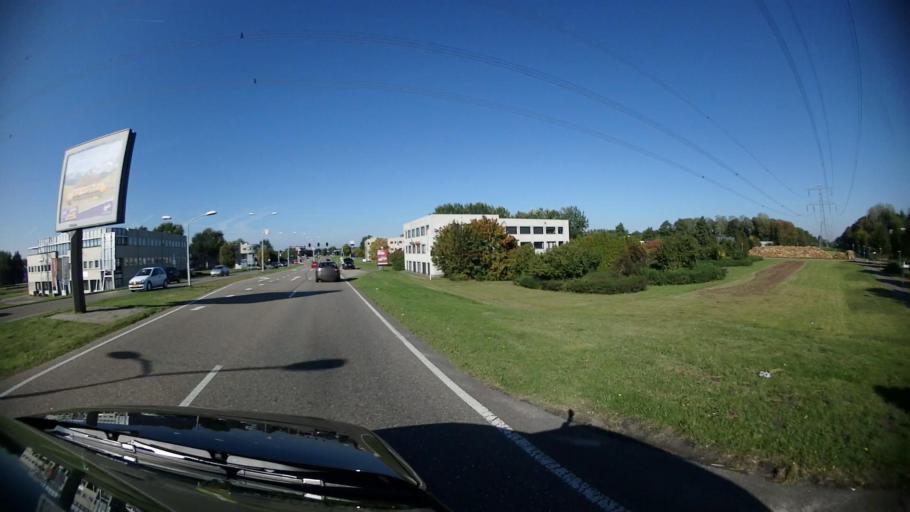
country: NL
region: Flevoland
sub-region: Gemeente Almere
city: Almere Stad
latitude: 52.3526
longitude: 5.1943
